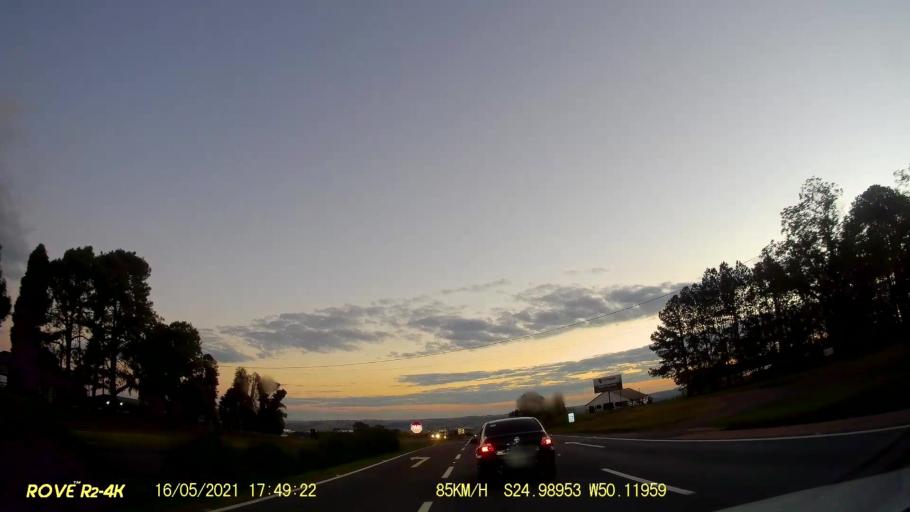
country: BR
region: Parana
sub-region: Carambei
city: Carambei
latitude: -24.9895
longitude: -50.1197
